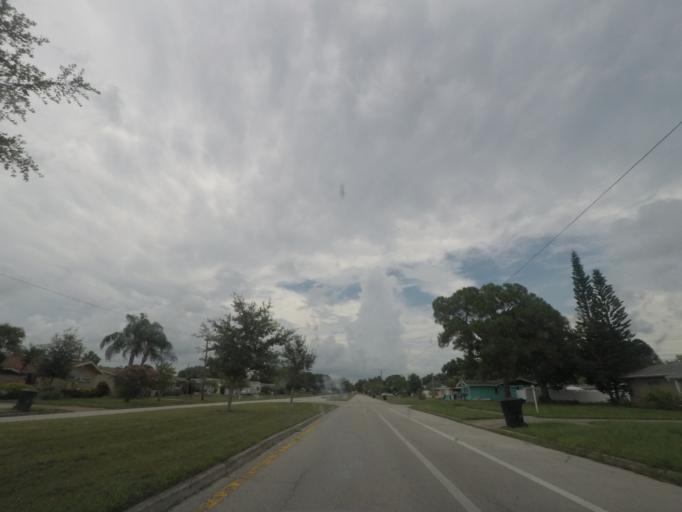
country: US
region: Florida
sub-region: Pinellas County
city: Kenneth City
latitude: 27.7990
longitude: -82.7153
